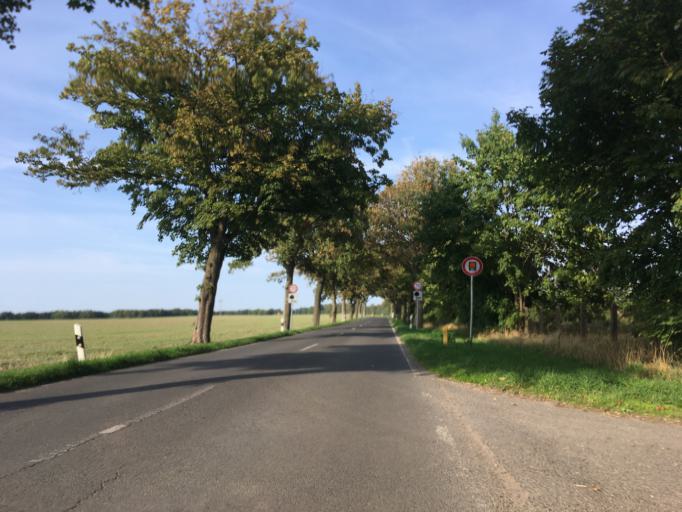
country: DE
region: Brandenburg
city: Brieskow-Finkenheerd
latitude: 52.2944
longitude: 14.5528
